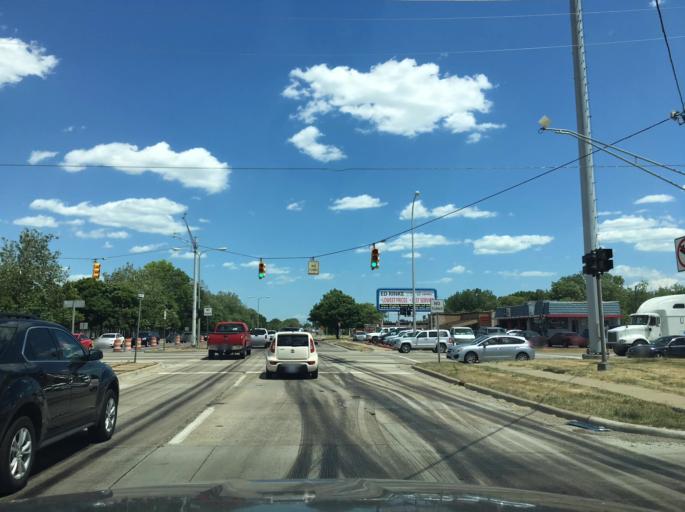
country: US
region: Michigan
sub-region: Macomb County
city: Center Line
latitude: 42.5061
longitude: -83.0468
